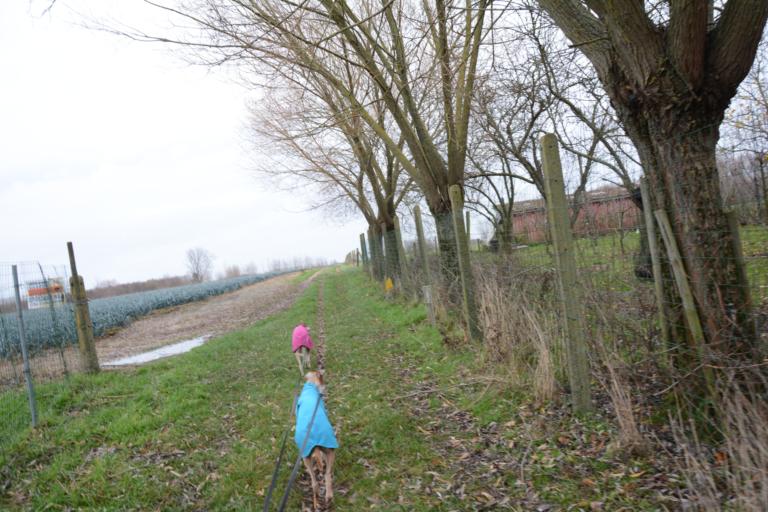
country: BE
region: Flanders
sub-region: Provincie Vlaams-Brabant
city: Opwijk
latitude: 50.9485
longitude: 4.1533
